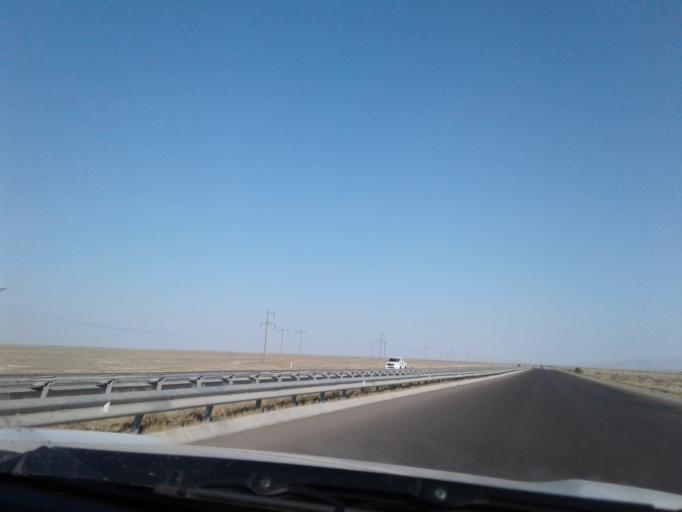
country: TM
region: Balkan
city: Serdar
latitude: 39.0799
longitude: 56.0542
